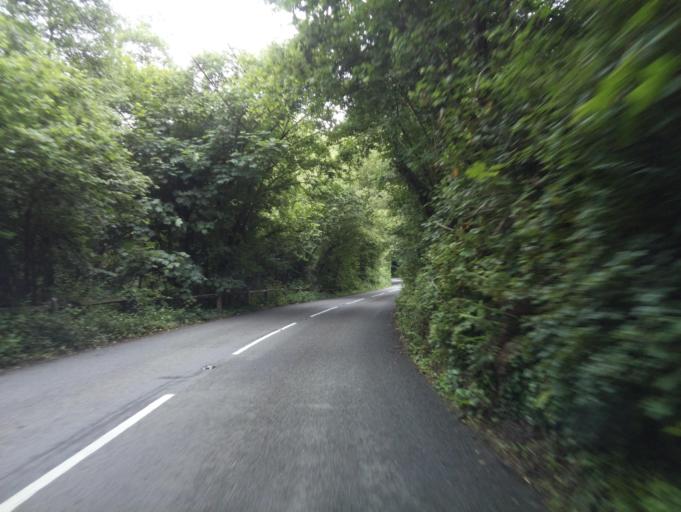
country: GB
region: England
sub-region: Devon
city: Chudleigh
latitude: 50.6494
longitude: -3.6411
